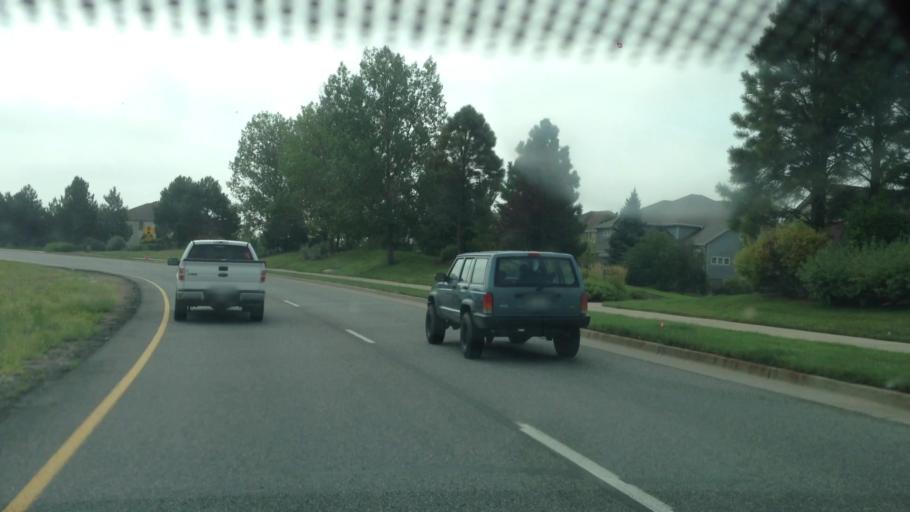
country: US
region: Colorado
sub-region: Douglas County
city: Parker
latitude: 39.6018
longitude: -104.7254
